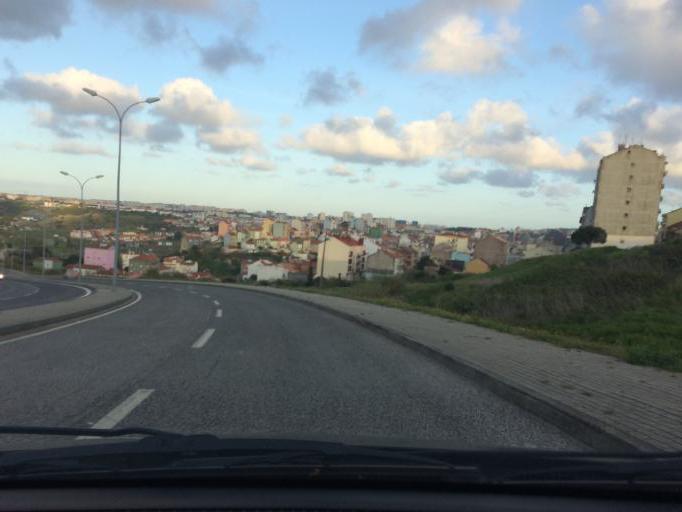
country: PT
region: Lisbon
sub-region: Odivelas
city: Famoes
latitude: 38.7719
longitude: -9.2193
